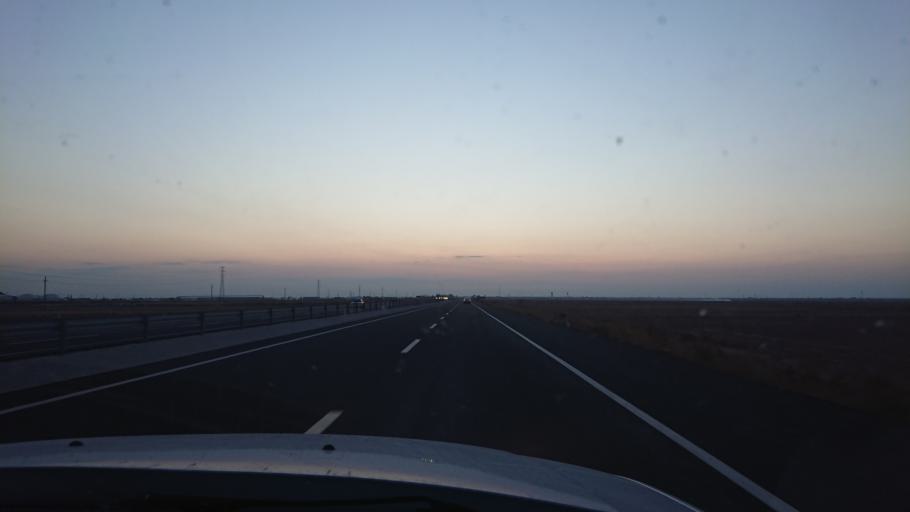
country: TR
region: Aksaray
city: Yesilova
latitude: 38.3007
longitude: 33.7969
